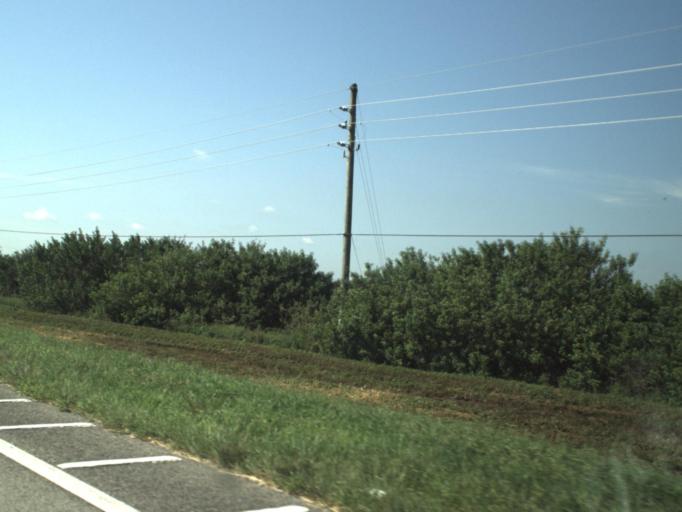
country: US
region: Florida
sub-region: Palm Beach County
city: Belle Glade Camp
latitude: 26.5560
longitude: -80.7098
